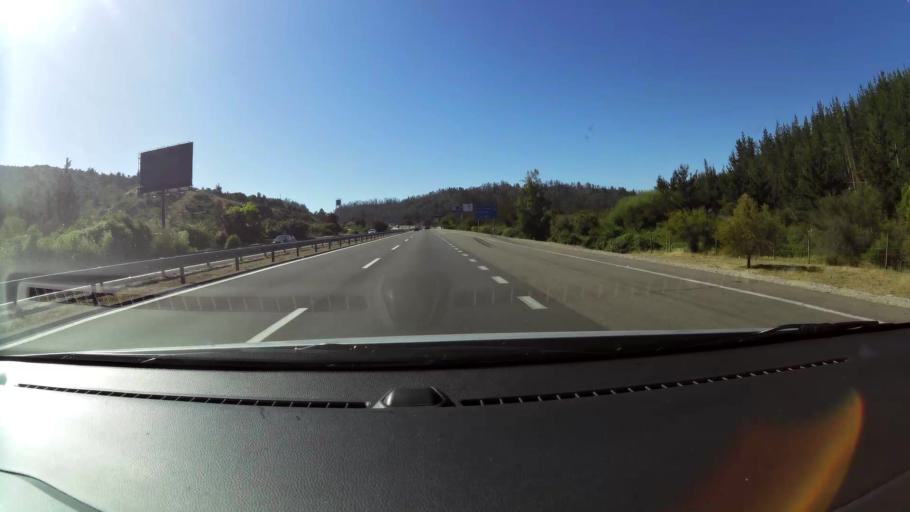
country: CL
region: Valparaiso
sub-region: Provincia de Marga Marga
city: Quilpue
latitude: -33.2187
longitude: -71.4721
